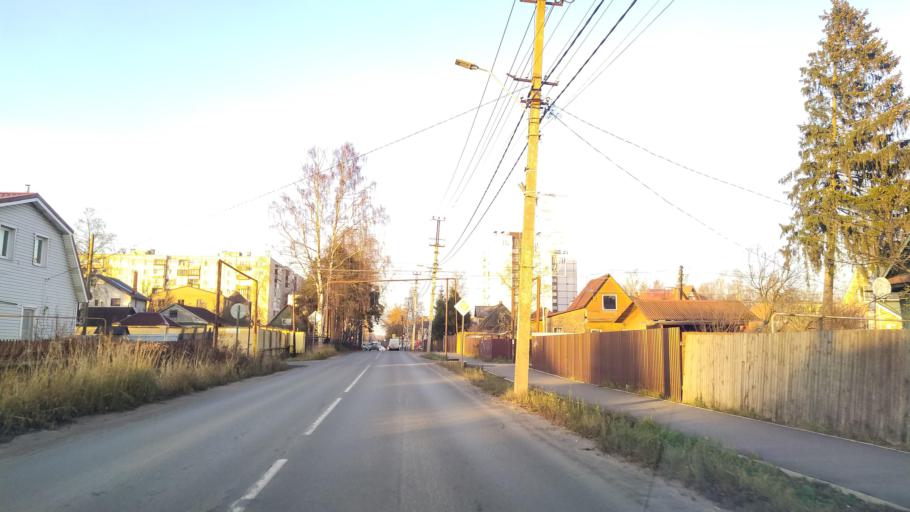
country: RU
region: Leningrad
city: Vsevolozhsk
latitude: 60.0216
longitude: 30.6323
